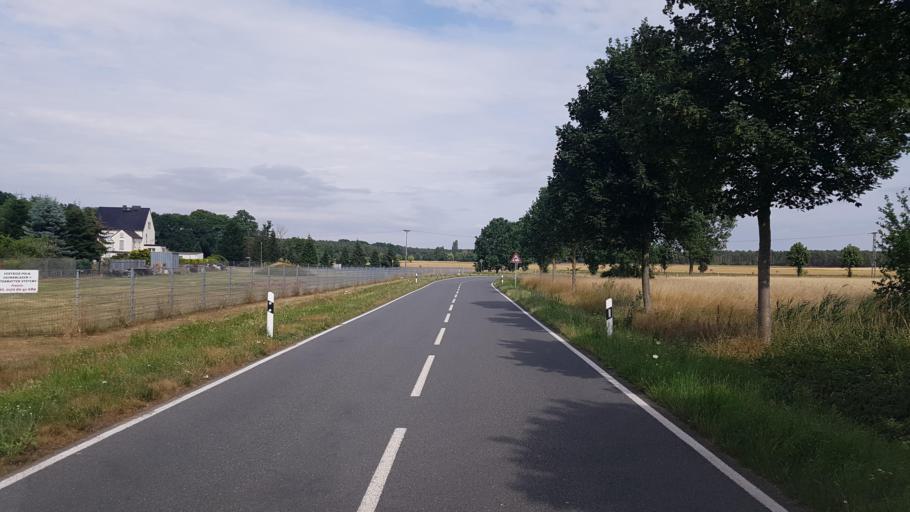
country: DE
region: Saxony-Anhalt
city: Abtsdorf
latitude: 51.8890
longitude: 12.7529
